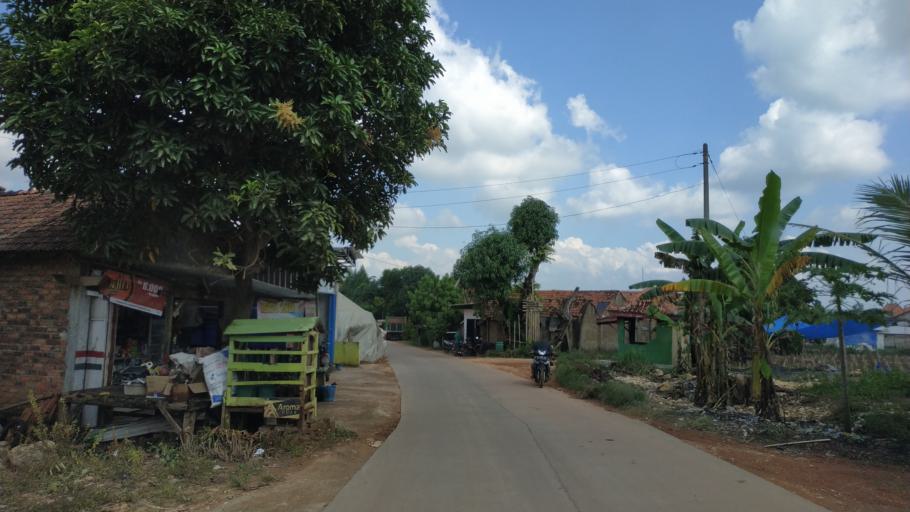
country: ID
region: Central Java
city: Guyangan
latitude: -7.0066
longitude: 111.1129
